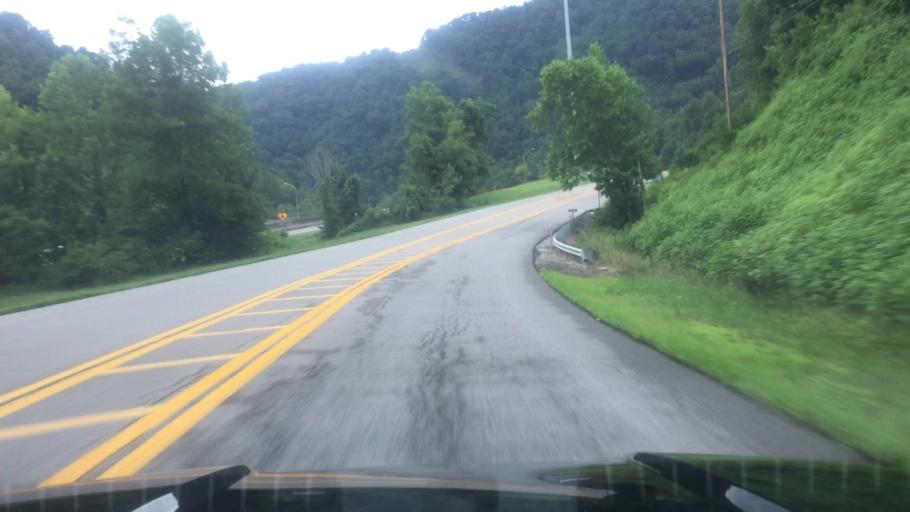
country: US
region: West Virginia
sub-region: Kanawha County
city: Montgomery
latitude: 38.1260
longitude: -81.3874
